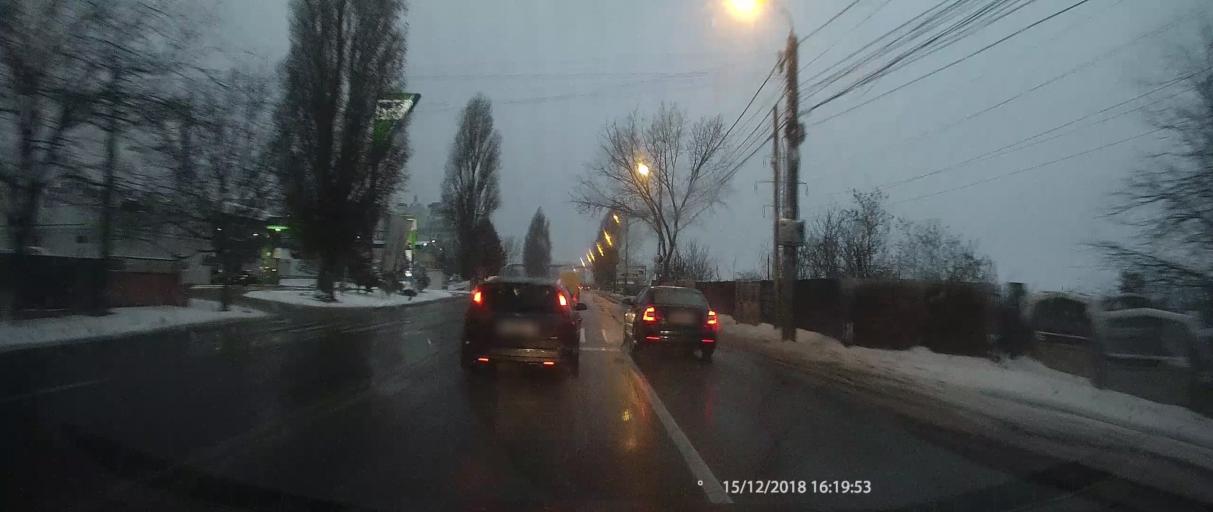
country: RO
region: Galati
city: Galati
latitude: 45.4171
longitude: 28.0049
